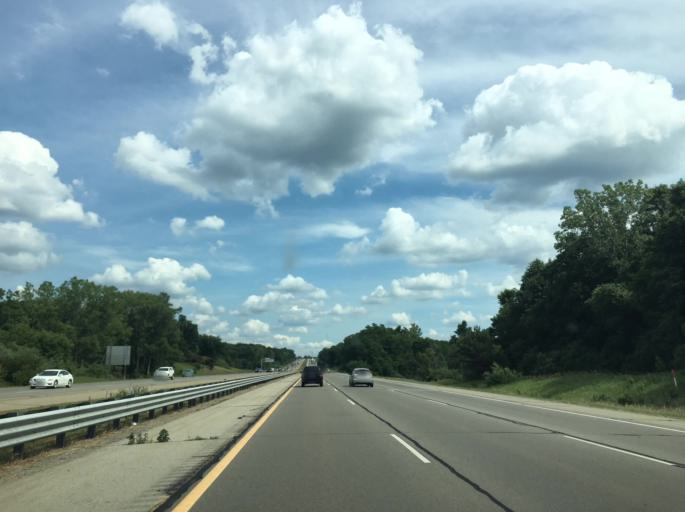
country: US
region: Michigan
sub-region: Oakland County
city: Holly
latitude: 42.8021
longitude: -83.5579
